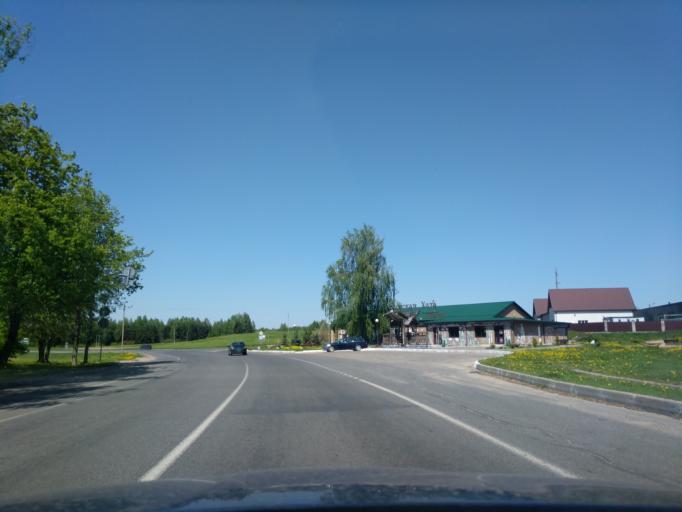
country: BY
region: Minsk
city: Myadzyel
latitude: 54.8848
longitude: 26.9374
